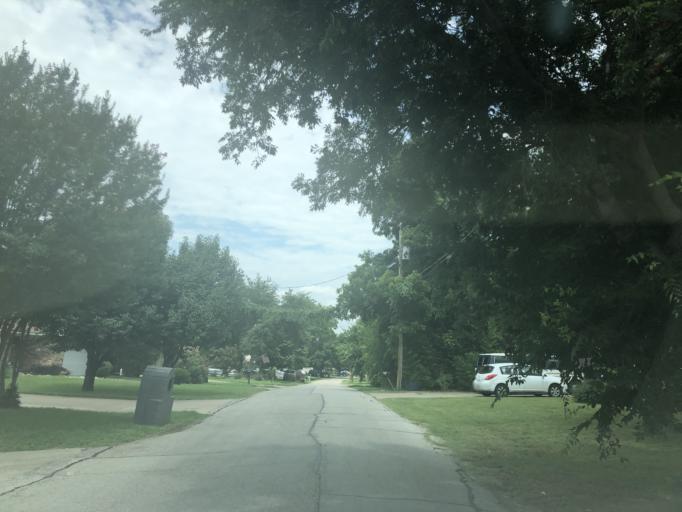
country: US
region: Texas
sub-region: Dallas County
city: Irving
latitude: 32.7879
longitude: -96.9351
